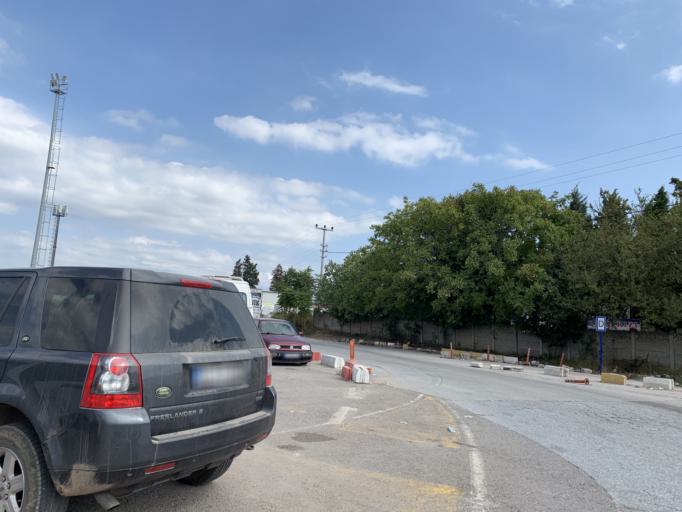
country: TR
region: Yalova
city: Taskopru
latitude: 40.6926
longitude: 29.4464
